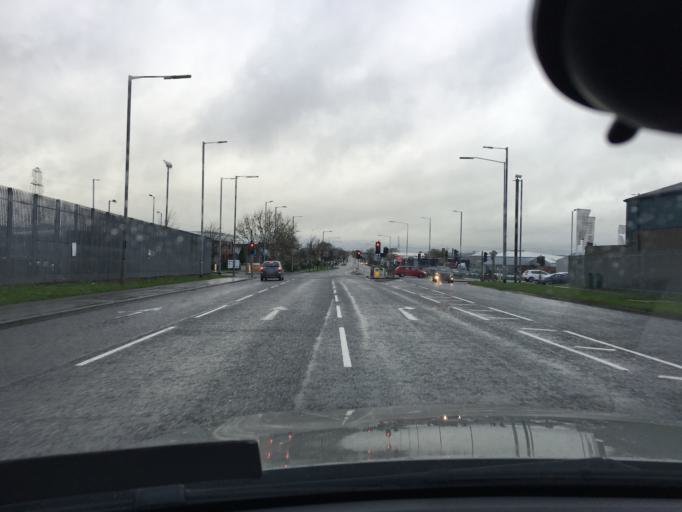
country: GB
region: Northern Ireland
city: Carnmoney
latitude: 54.6735
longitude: -5.9811
